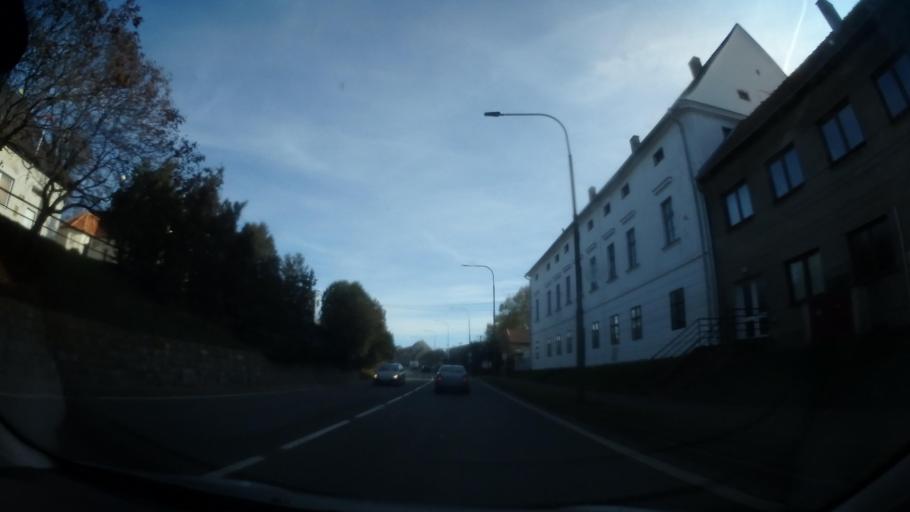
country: CZ
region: South Moravian
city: Sardice
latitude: 49.0095
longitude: 17.0462
